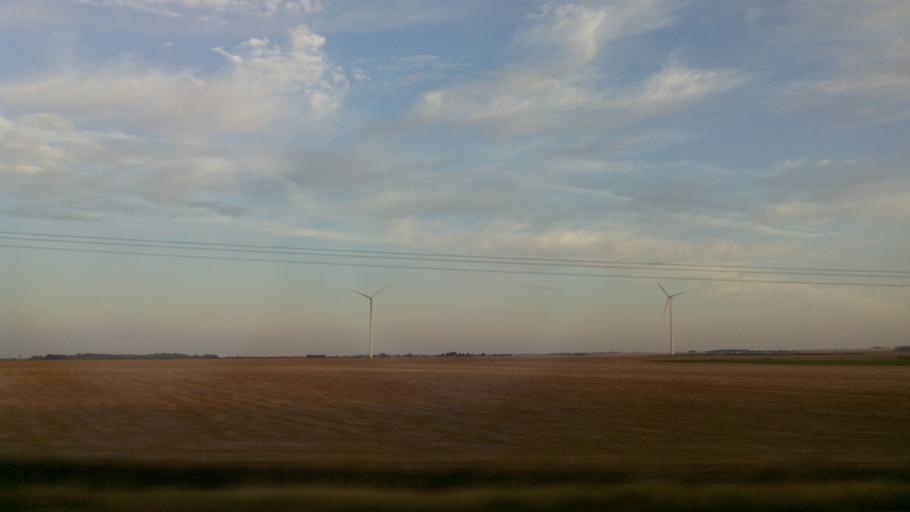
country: FR
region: Centre
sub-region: Departement d'Eure-et-Loir
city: Bonneval
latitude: 48.2120
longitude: 1.4213
